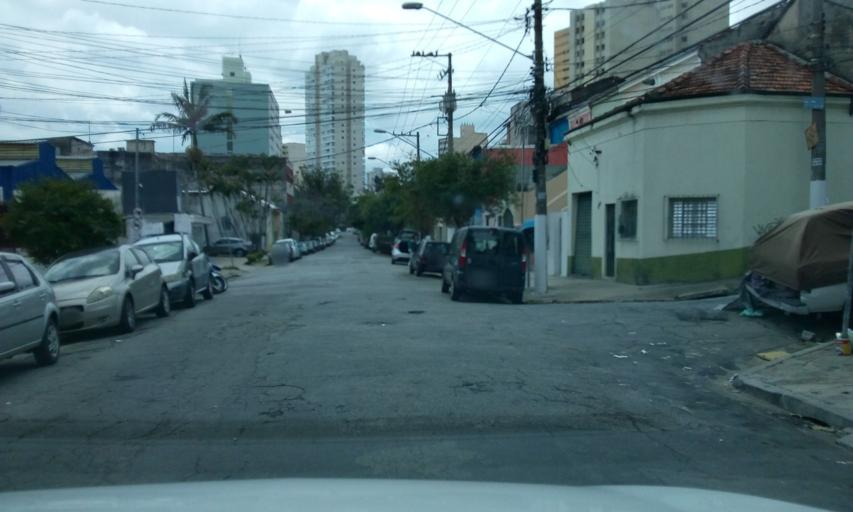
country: BR
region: Sao Paulo
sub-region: Sao Paulo
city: Sao Paulo
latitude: -23.5672
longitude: -46.6251
